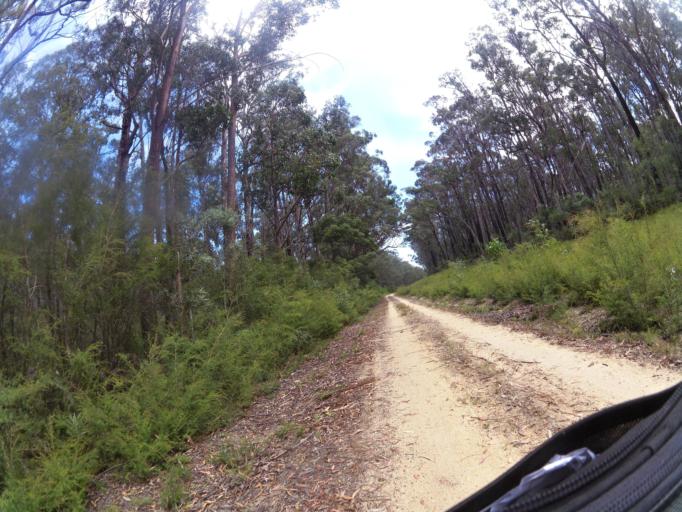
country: AU
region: Victoria
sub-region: East Gippsland
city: Lakes Entrance
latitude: -37.7401
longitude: 148.0157
